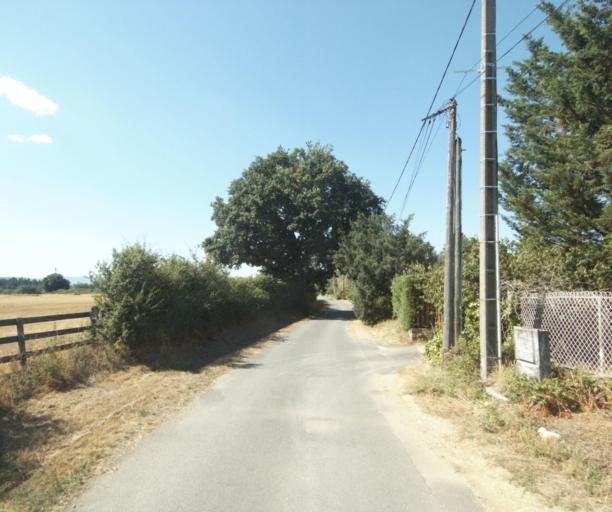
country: FR
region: Rhone-Alpes
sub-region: Departement du Rhone
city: Lozanne
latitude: 45.8397
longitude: 4.7043
